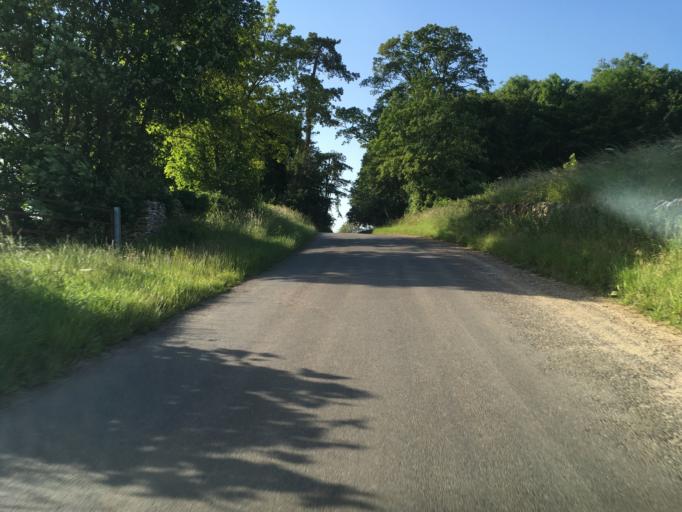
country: GB
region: England
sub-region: Gloucestershire
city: Lechlade
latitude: 51.7561
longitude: -1.7215
